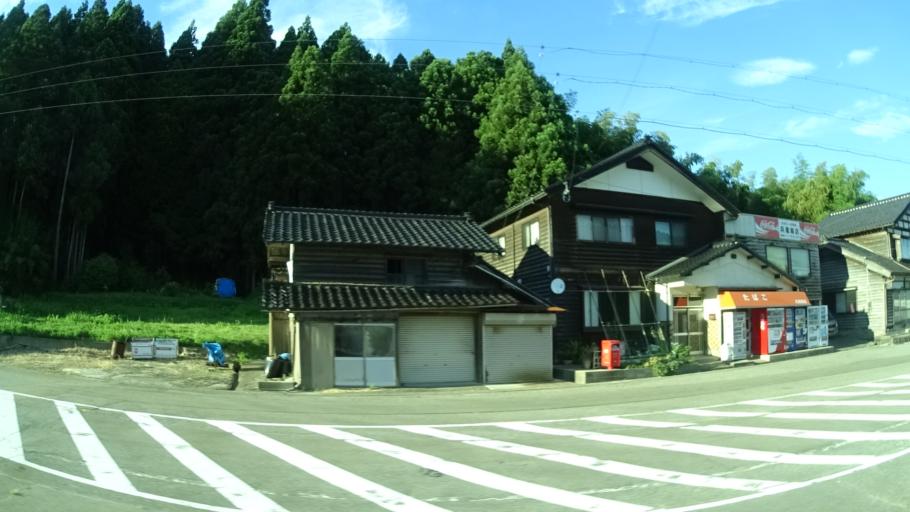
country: JP
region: Ishikawa
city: Nanao
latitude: 37.2490
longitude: 136.8913
